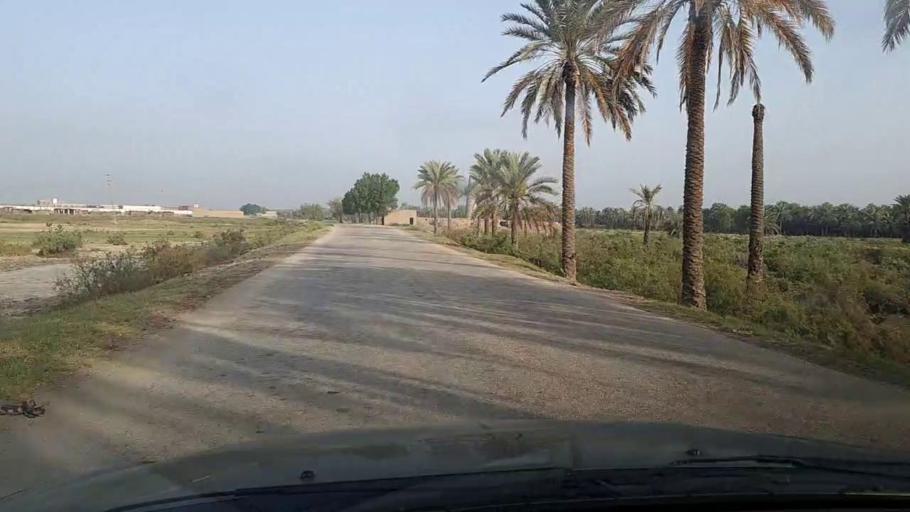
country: PK
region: Sindh
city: Khairpur
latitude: 27.5451
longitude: 68.7021
